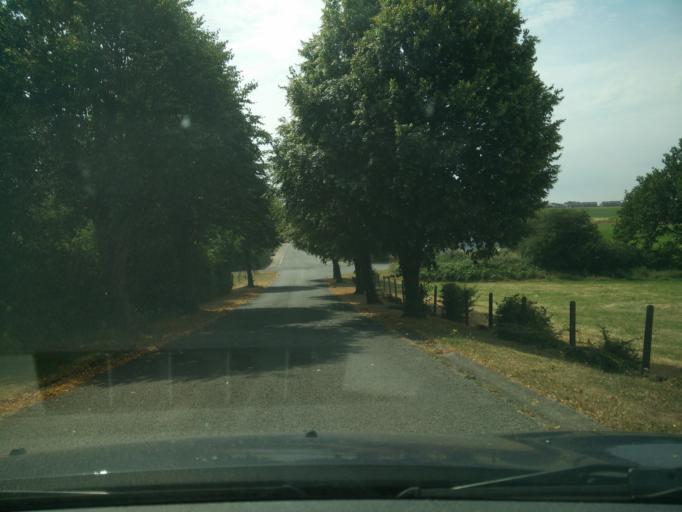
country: BE
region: Wallonia
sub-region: Province du Brabant Wallon
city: Tubize
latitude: 50.6984
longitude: 4.2314
